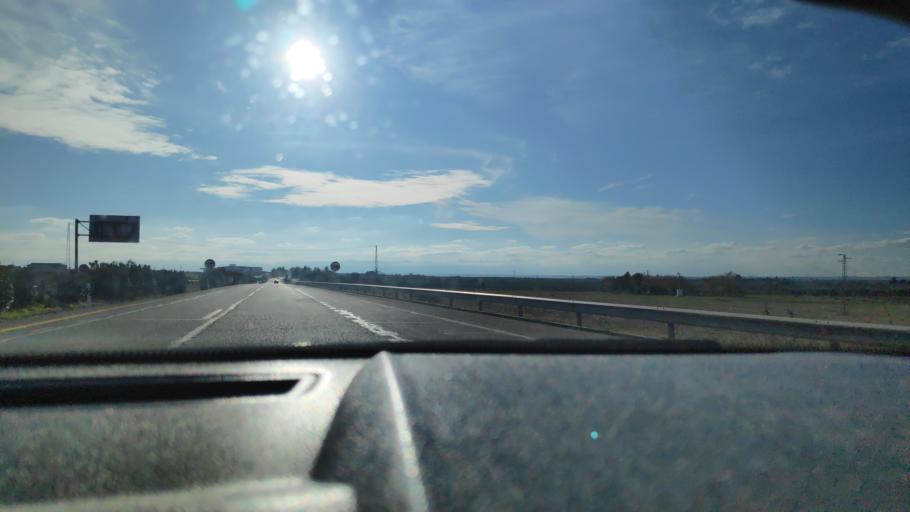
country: ES
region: Andalusia
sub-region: Provincia de Sevilla
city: Ecija
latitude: 37.5845
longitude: -4.9901
